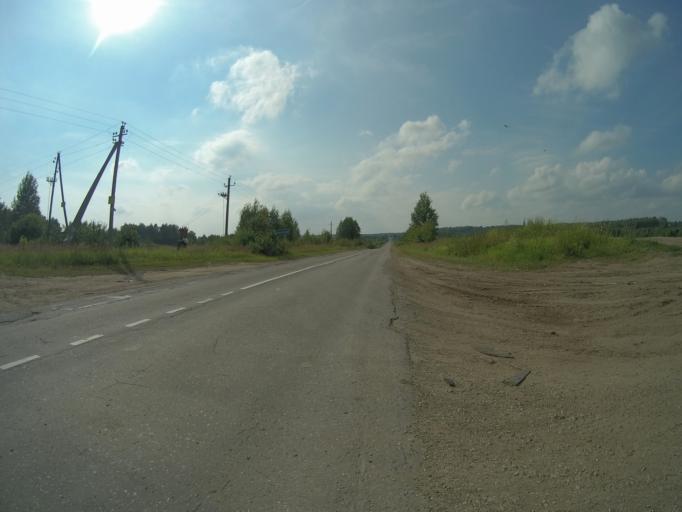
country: RU
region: Vladimir
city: Vorsha
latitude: 56.0051
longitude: 40.1826
